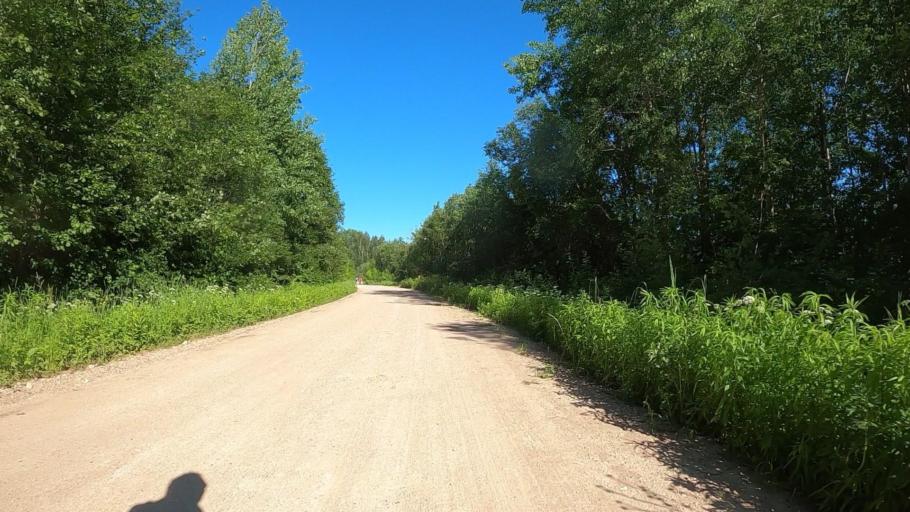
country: LV
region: Ogre
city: Ogre
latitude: 56.7812
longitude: 24.6561
